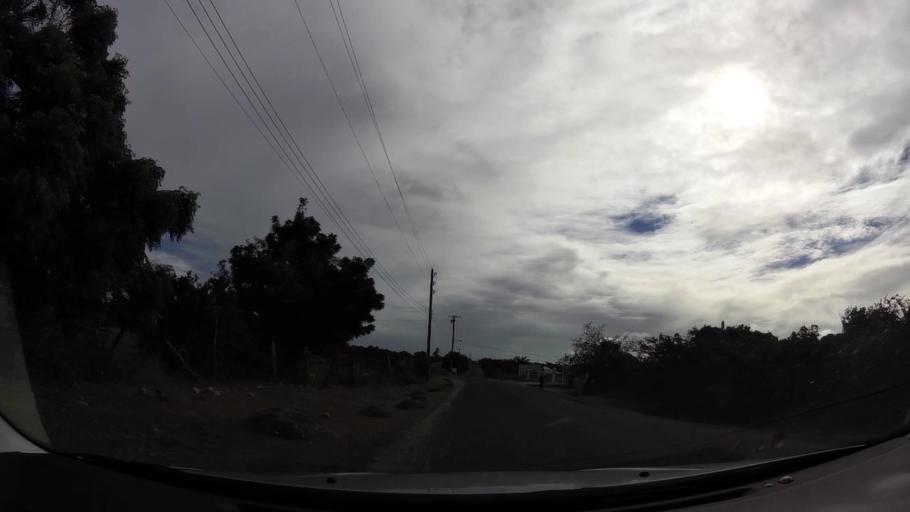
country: AG
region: Saint Peter
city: Parham
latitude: 17.0842
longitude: -61.7175
